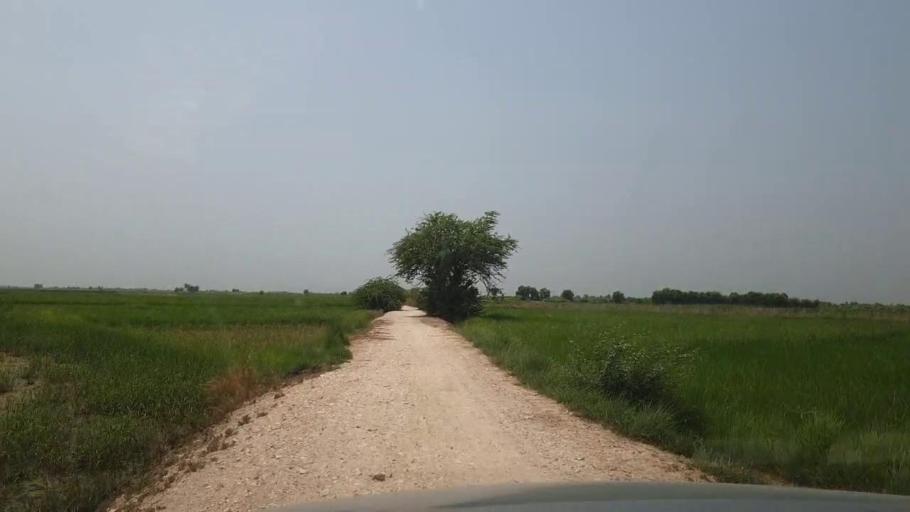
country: PK
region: Sindh
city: Garhi Yasin
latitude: 27.8737
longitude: 68.4938
